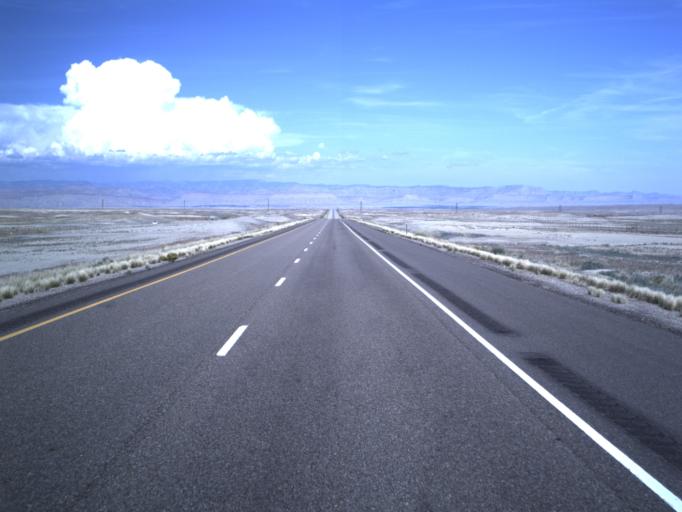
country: US
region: Utah
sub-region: Carbon County
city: East Carbon City
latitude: 38.9587
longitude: -110.2941
